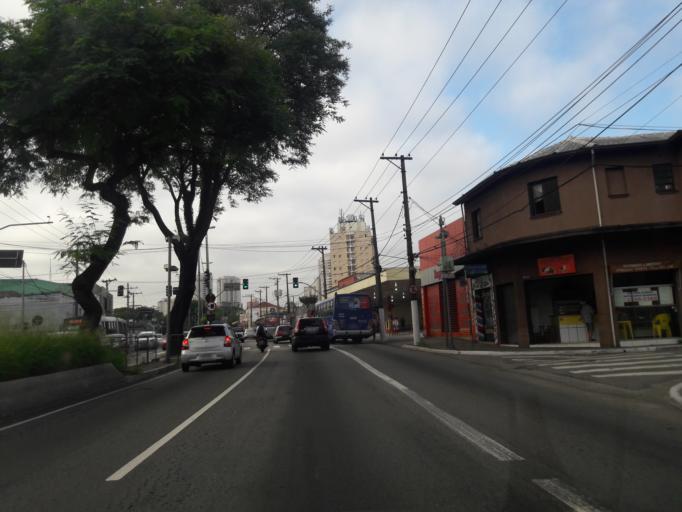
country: BR
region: Sao Paulo
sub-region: Sao Caetano Do Sul
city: Sao Caetano do Sul
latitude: -23.6167
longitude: -46.6016
